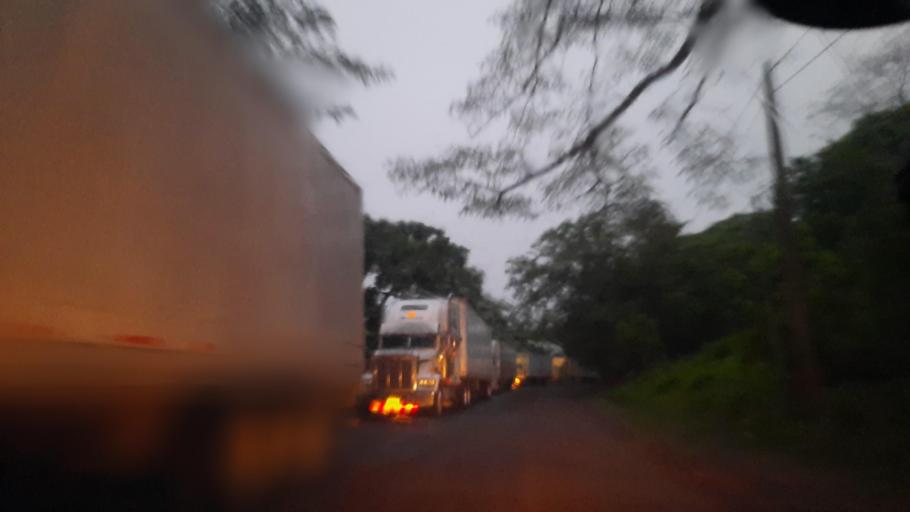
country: GT
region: Jutiapa
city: Atescatempa
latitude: 14.2201
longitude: -89.6955
